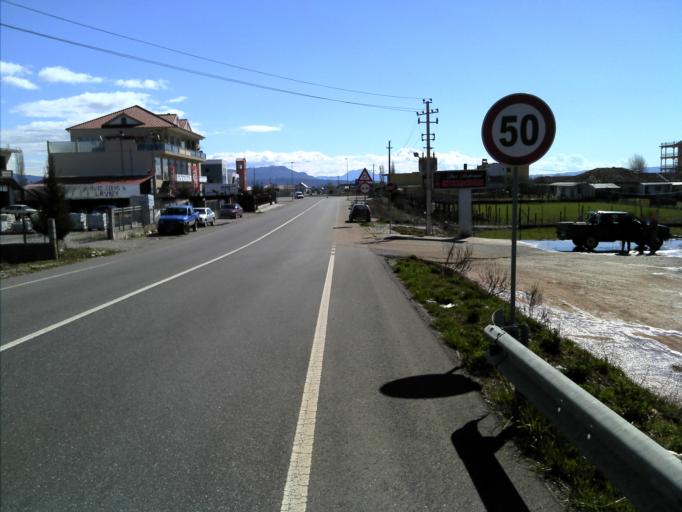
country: AL
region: Shkoder
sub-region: Rrethi i Malesia e Madhe
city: Grude-Fushe
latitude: 42.1352
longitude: 19.4871
